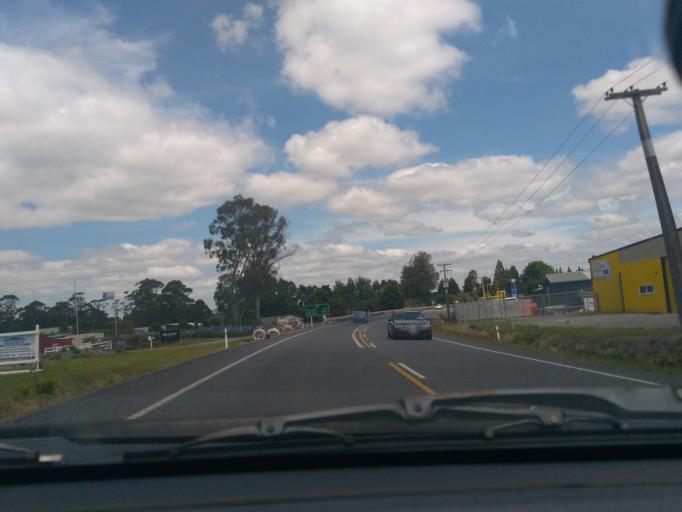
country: NZ
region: Northland
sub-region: Far North District
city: Kerikeri
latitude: -35.2082
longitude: 173.9196
